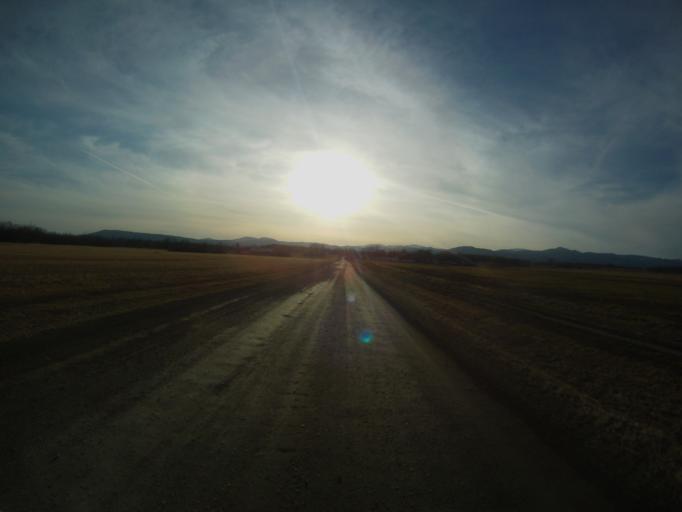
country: US
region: New York
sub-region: Essex County
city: Port Henry
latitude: 44.0538
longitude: -73.3689
